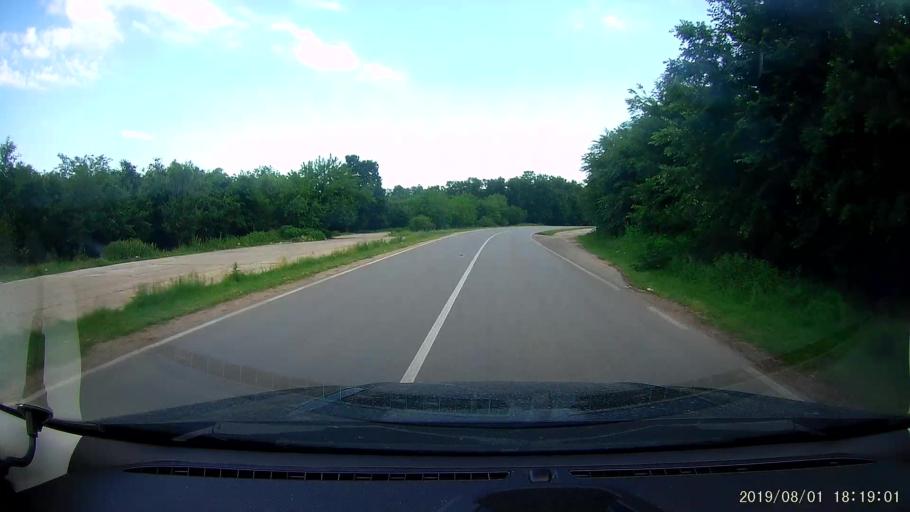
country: BG
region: Shumen
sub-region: Obshtina Kaolinovo
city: Kaolinovo
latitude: 43.6893
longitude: 27.0875
